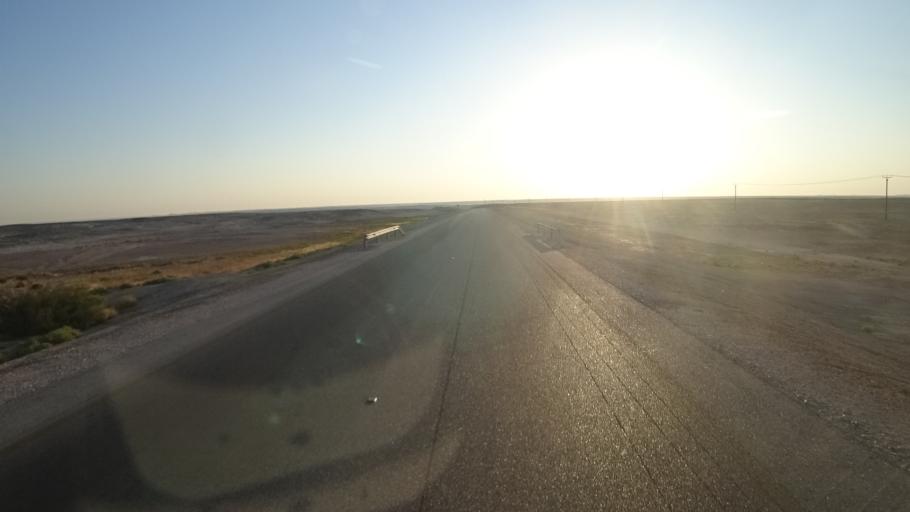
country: OM
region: Zufar
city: Salalah
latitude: 17.5363
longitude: 53.4085
